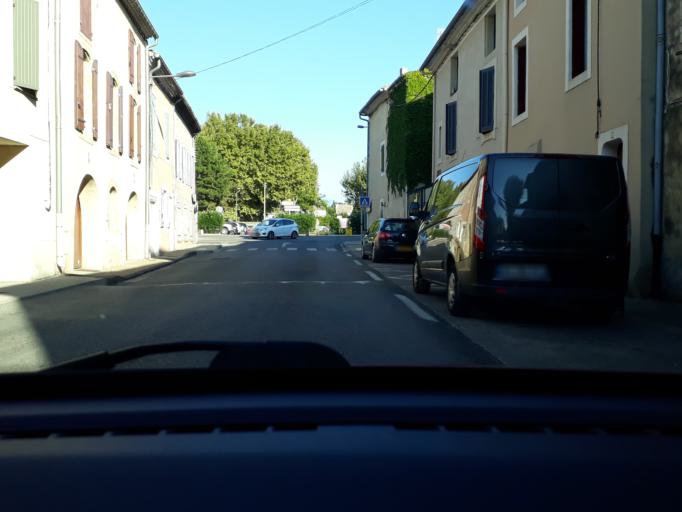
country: FR
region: Provence-Alpes-Cote d'Azur
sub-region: Departement du Vaucluse
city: Sainte-Cecile-les-Vignes
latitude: 44.2467
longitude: 4.8851
